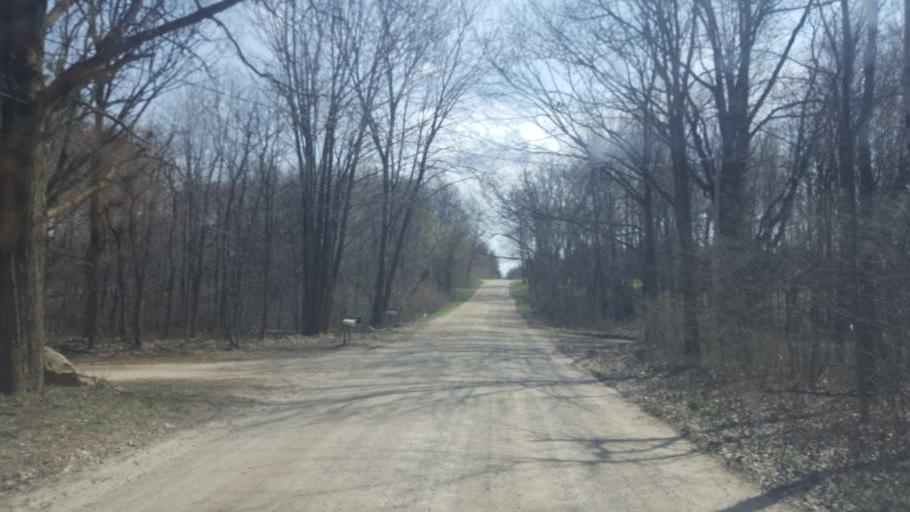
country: US
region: Michigan
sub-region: Montcalm County
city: Edmore
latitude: 43.4592
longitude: -84.9285
